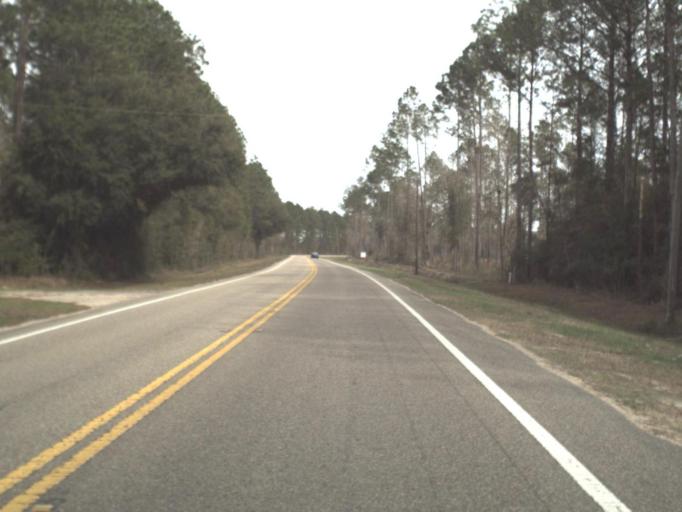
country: US
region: Florida
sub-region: Leon County
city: Woodville
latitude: 30.2258
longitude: -84.2118
